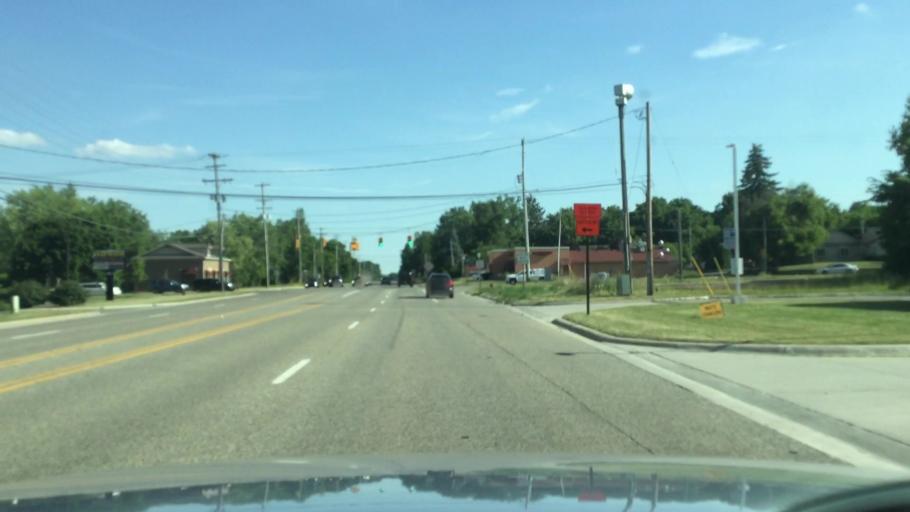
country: US
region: Michigan
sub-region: Genesee County
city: Grand Blanc
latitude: 42.8883
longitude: -83.5994
